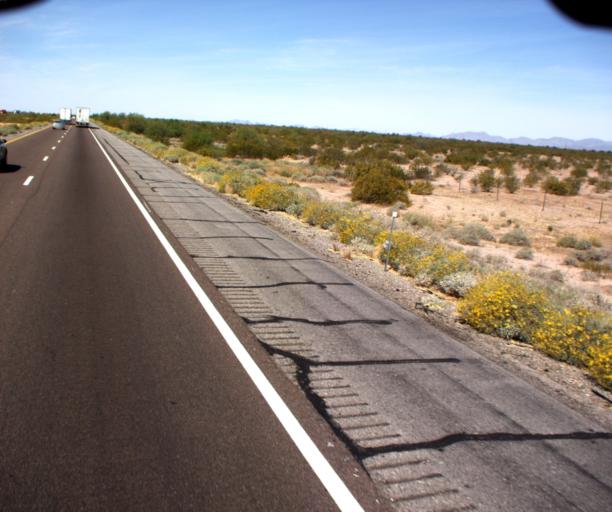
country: US
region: Arizona
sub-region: La Paz County
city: Salome
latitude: 33.5485
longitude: -113.2161
